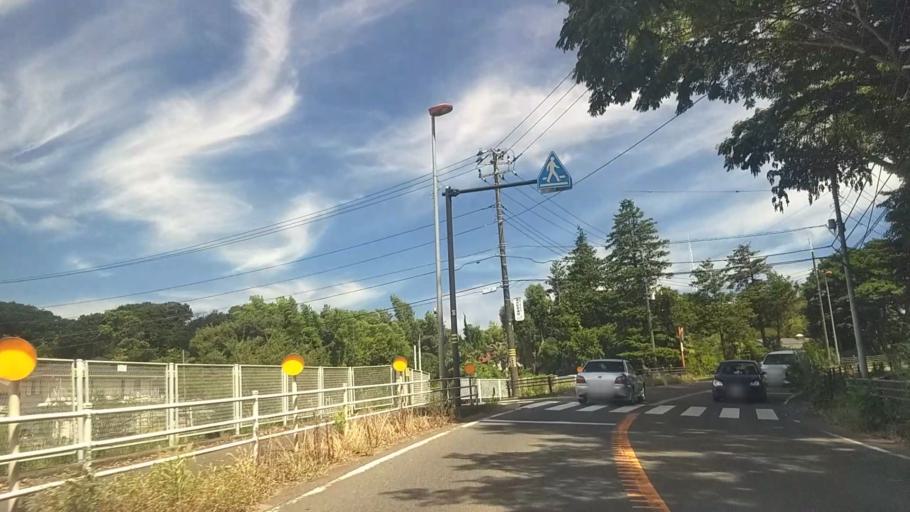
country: JP
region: Kanagawa
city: Miura
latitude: 35.2075
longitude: 139.6463
